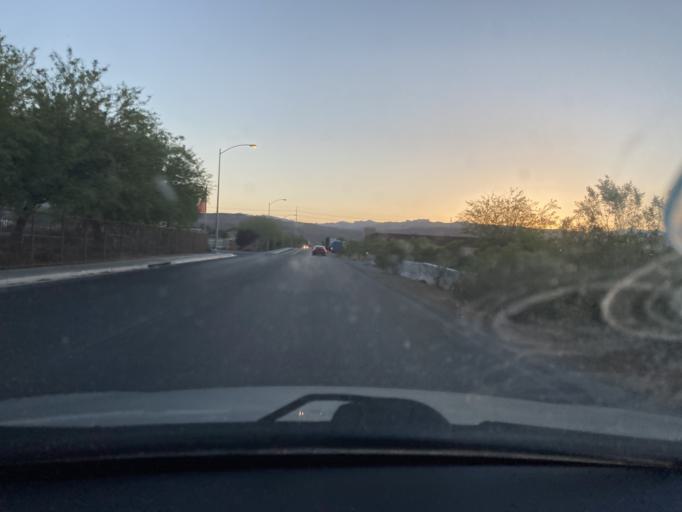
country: US
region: Nevada
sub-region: Clark County
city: Enterprise
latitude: 36.0593
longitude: -115.2739
